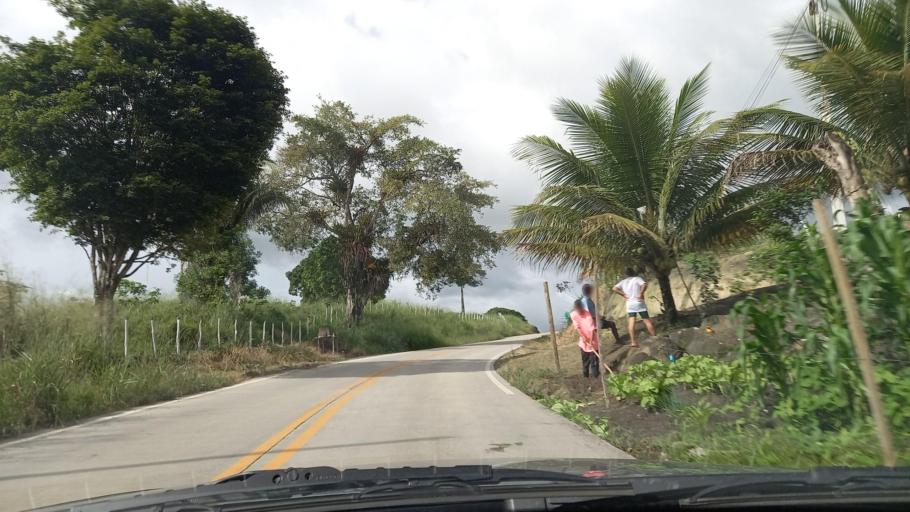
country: BR
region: Pernambuco
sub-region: Maraial
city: Maraial
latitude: -8.7905
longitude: -35.8829
